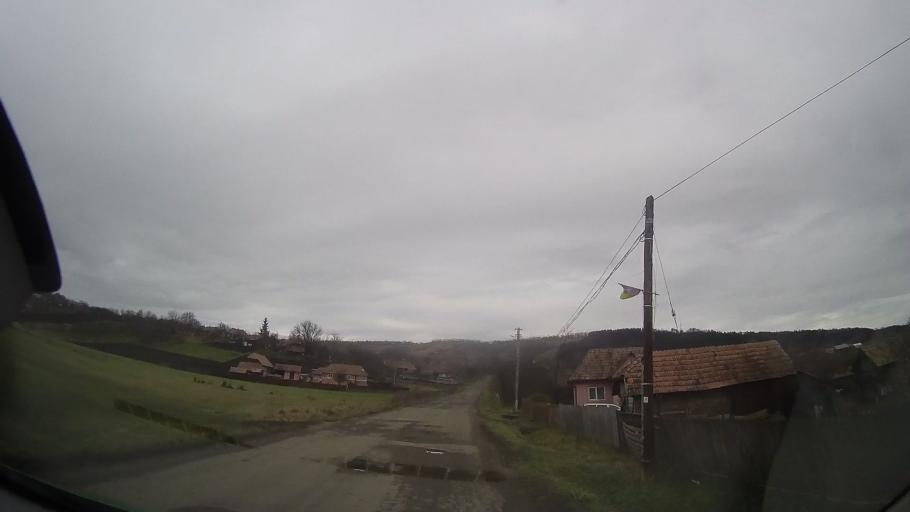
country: RO
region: Mures
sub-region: Comuna Bala
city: Bala
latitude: 46.7085
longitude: 24.5013
